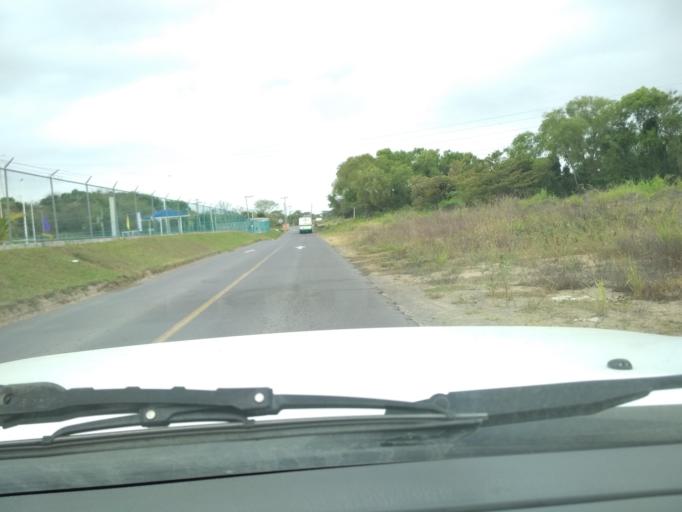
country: MX
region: Veracruz
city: Boca del Rio
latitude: 19.0898
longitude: -96.1219
